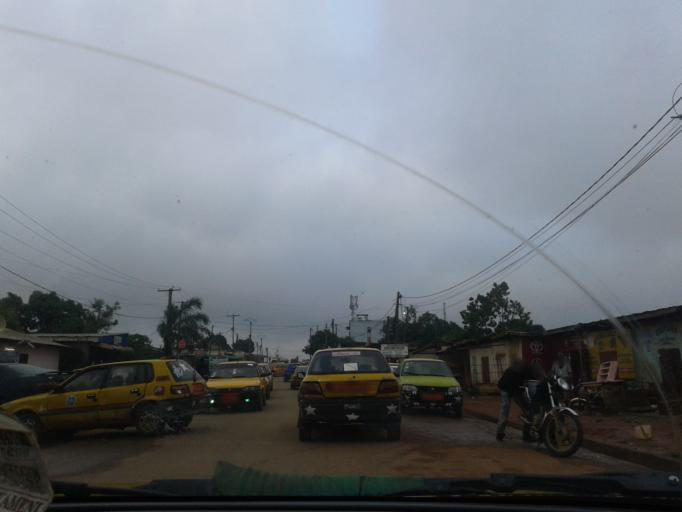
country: CM
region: Centre
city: Yaounde
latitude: 3.8958
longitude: 11.5301
